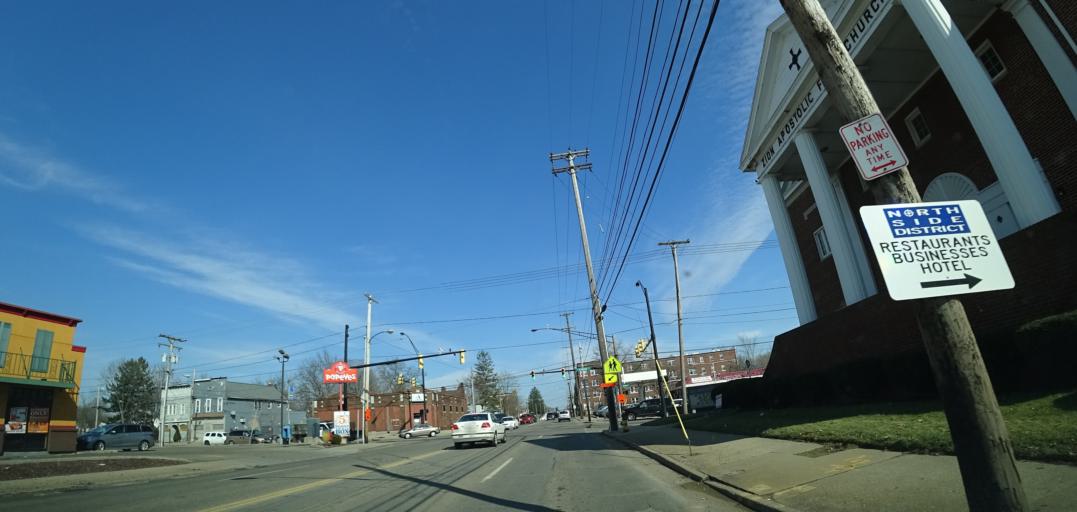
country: US
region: Ohio
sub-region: Summit County
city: Akron
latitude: 41.1021
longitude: -81.5158
